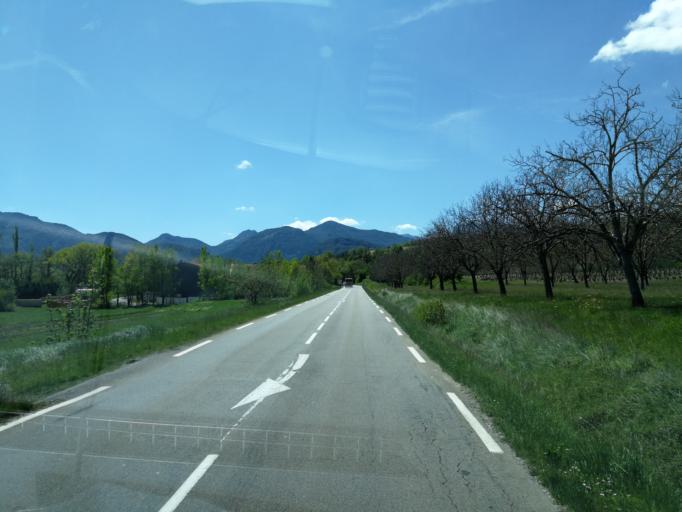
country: FR
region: Rhone-Alpes
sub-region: Departement de la Drome
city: Die
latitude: 44.7310
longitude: 5.2672
